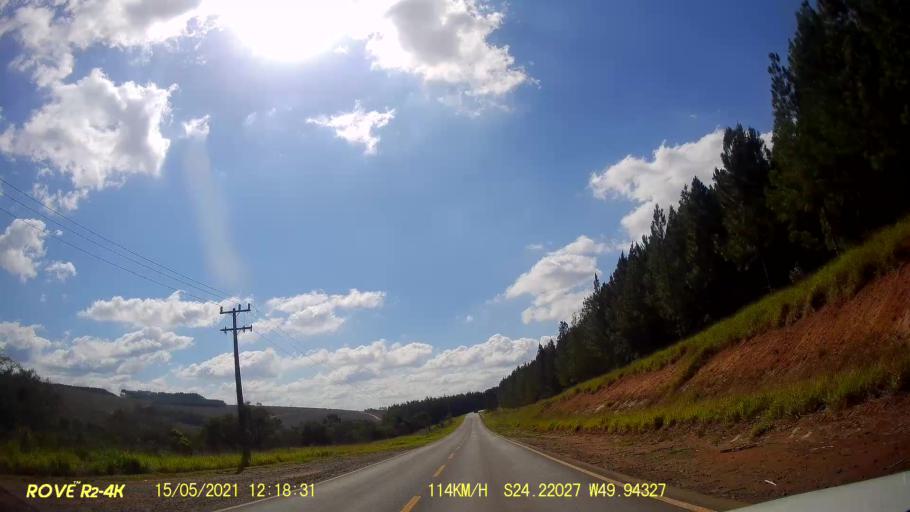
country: BR
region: Parana
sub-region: Jaguariaiva
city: Jaguariaiva
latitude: -24.2204
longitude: -49.9435
